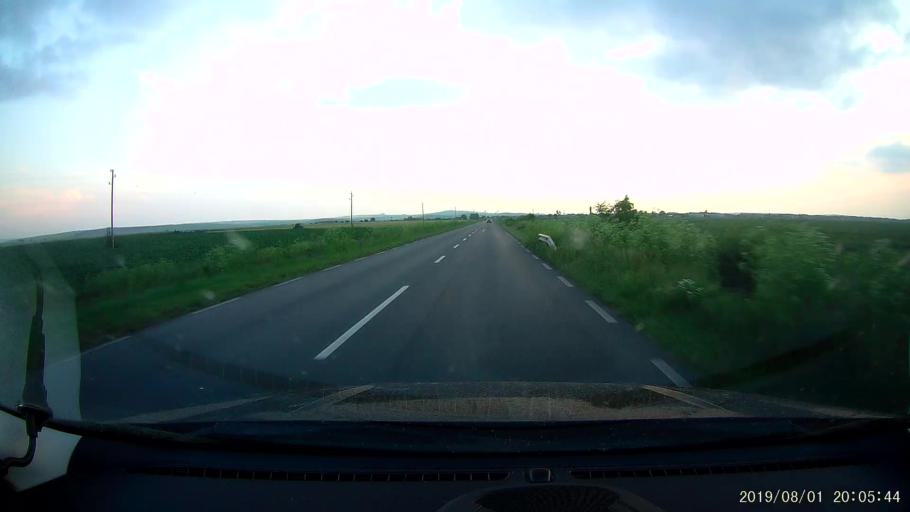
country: BG
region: Yambol
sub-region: Obshtina Yambol
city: Yambol
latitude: 42.5420
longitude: 26.5624
